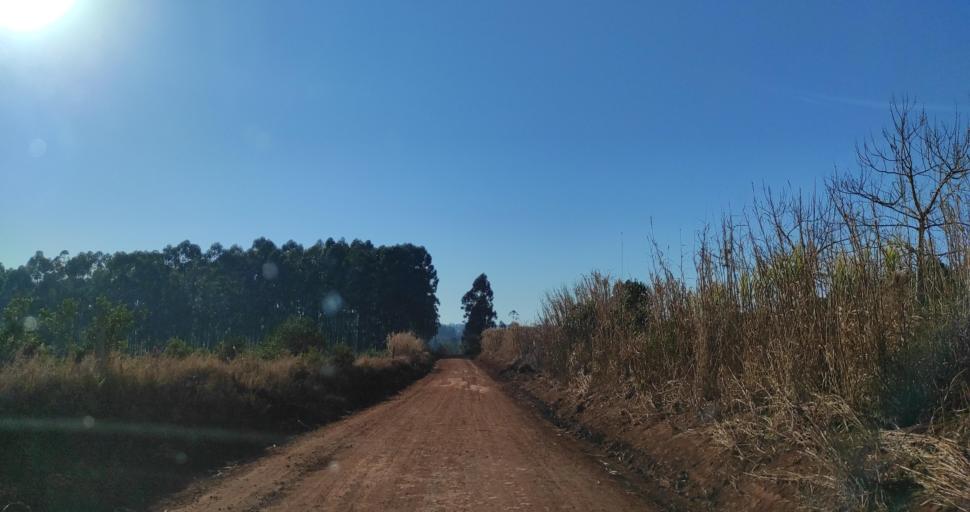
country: AR
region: Misiones
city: Capiovi
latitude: -26.8801
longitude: -55.0390
